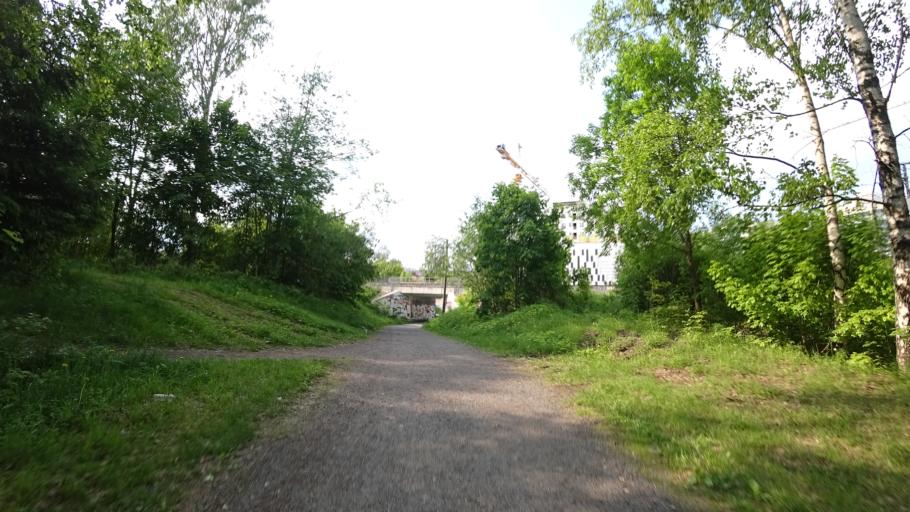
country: FI
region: Pirkanmaa
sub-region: Tampere
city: Pirkkala
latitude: 61.5030
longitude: 23.6304
